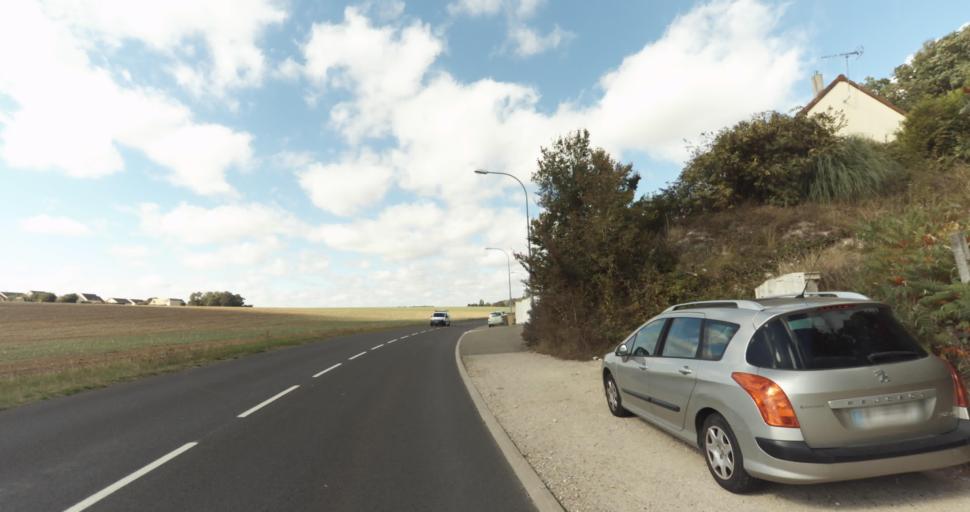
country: FR
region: Centre
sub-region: Departement d'Eure-et-Loir
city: Garnay
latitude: 48.7196
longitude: 1.3348
